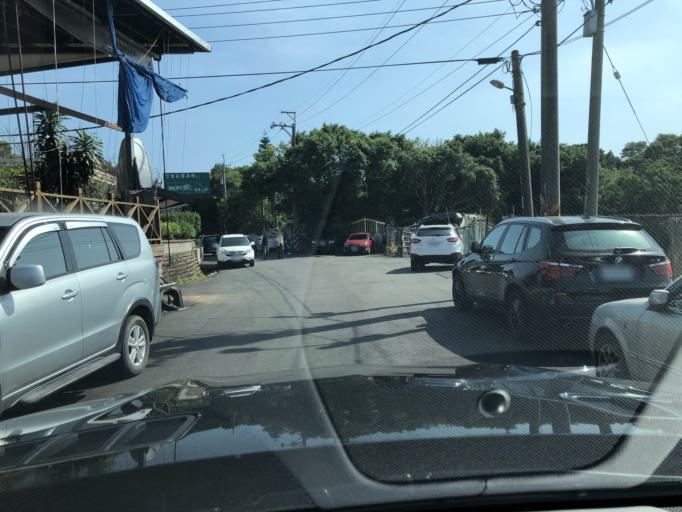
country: TW
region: Taiwan
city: Taoyuan City
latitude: 25.0653
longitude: 121.2937
